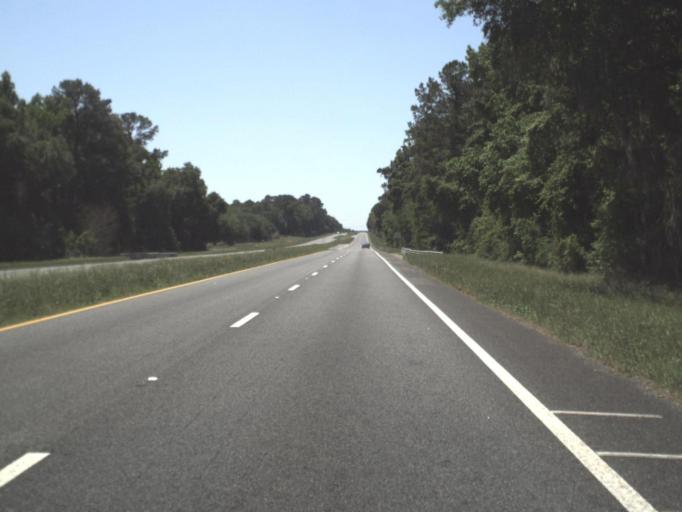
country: US
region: Florida
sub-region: Jefferson County
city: Monticello
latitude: 30.6553
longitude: -83.8772
